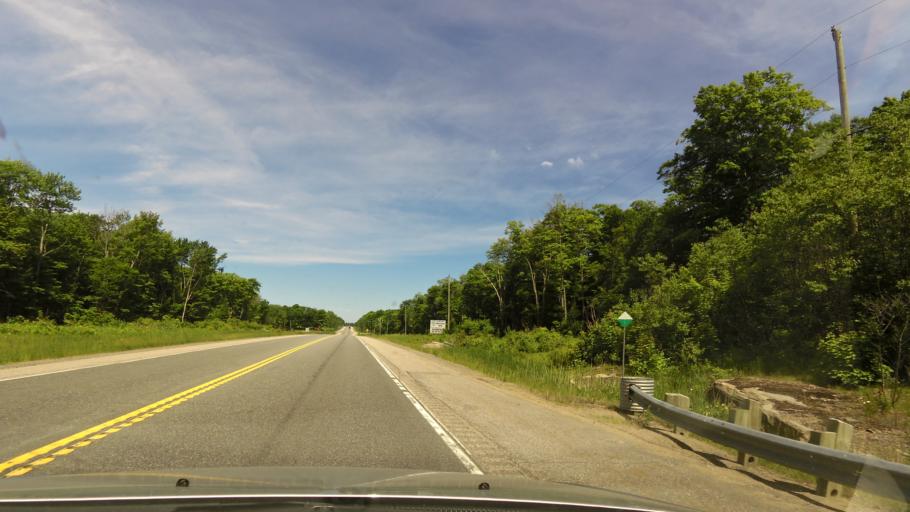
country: CA
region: Ontario
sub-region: Parry Sound District
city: Parry Sound
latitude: 45.4878
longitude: -80.1942
